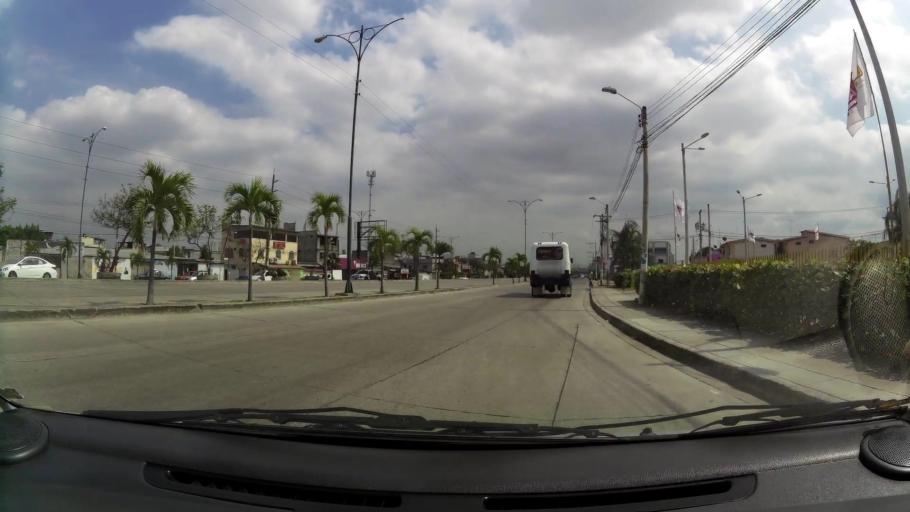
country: EC
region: Guayas
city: Eloy Alfaro
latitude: -2.0826
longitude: -79.9159
